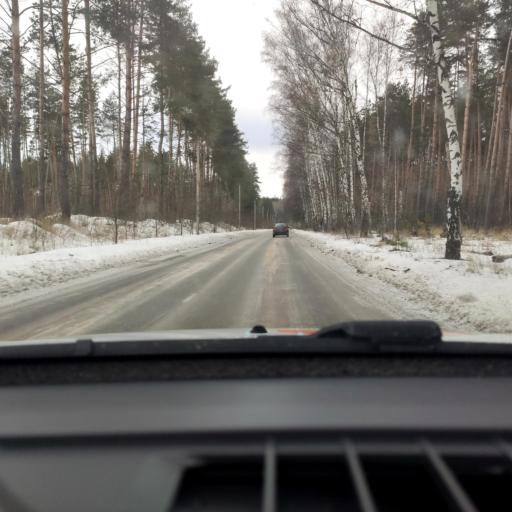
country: RU
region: Voronezj
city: Podgornoye
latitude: 51.7481
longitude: 39.1596
